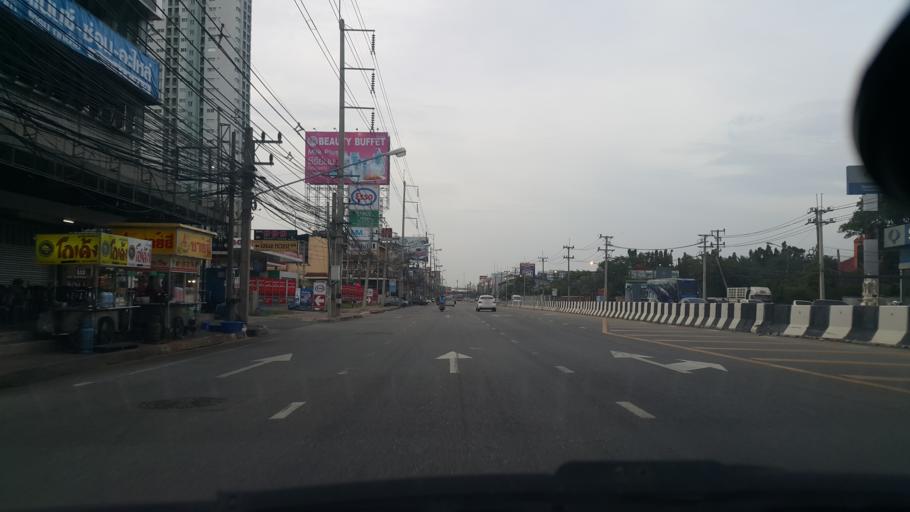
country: TH
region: Chon Buri
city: Phatthaya
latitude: 12.9625
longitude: 100.9091
